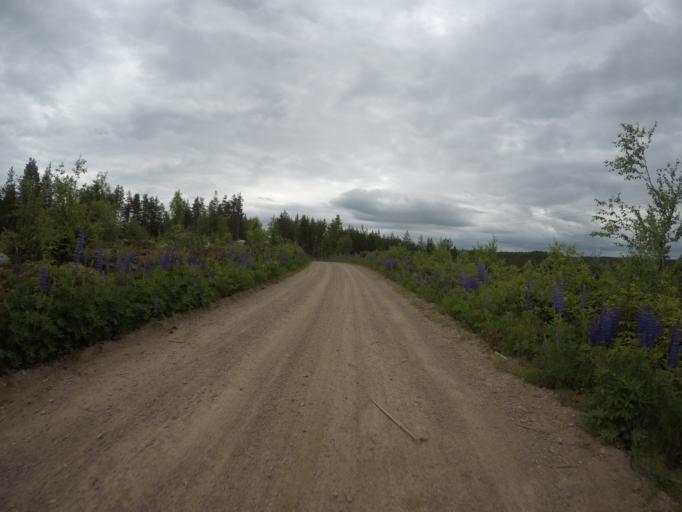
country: SE
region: Dalarna
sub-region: Ludvika Kommun
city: Abborrberget
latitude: 60.0885
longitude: 14.5496
